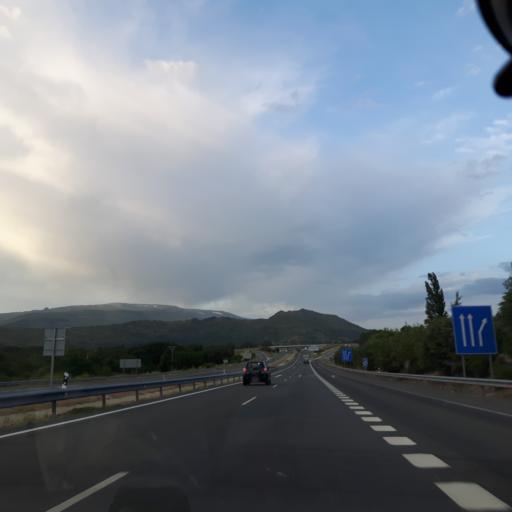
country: ES
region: Castille and Leon
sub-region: Provincia de Salamanca
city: Sorihuela
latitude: 40.4558
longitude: -5.6806
